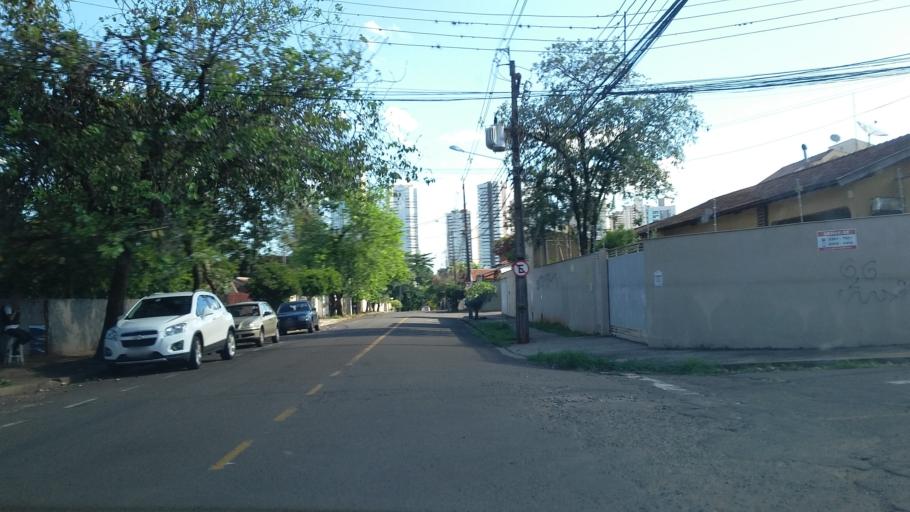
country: BR
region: Parana
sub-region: Londrina
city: Londrina
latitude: -23.3225
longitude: -51.1742
